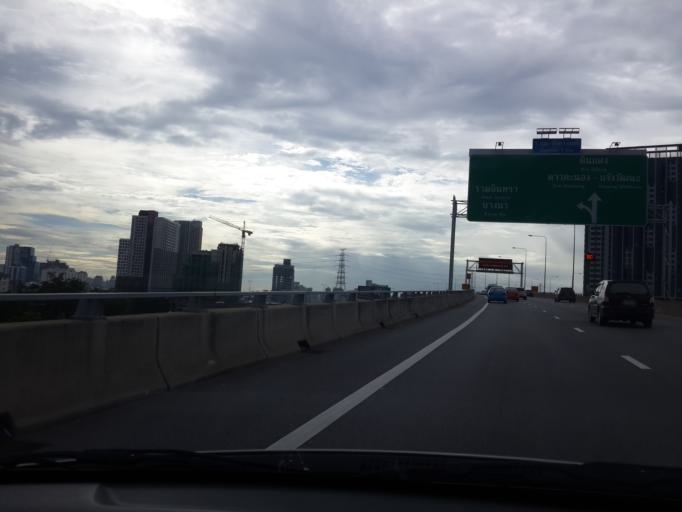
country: TH
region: Bangkok
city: Watthana
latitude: 13.7458
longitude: 100.6078
